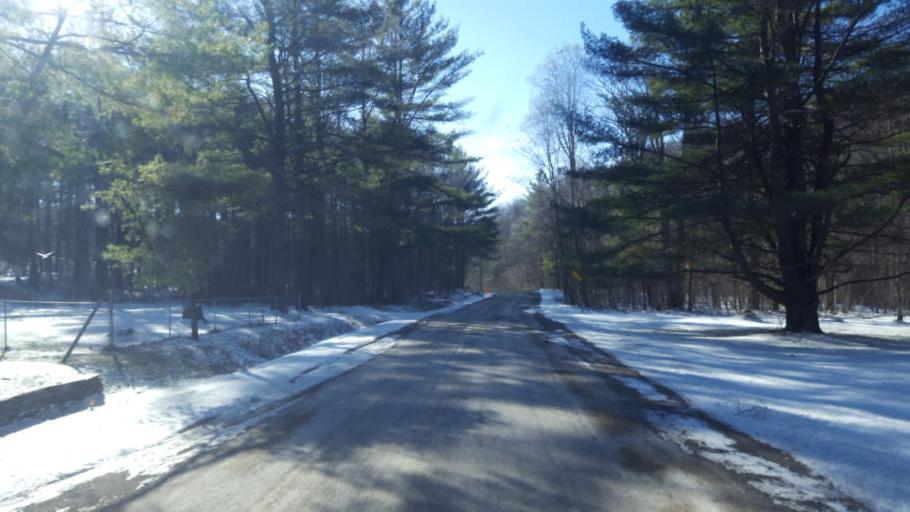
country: US
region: New York
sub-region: Allegany County
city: Wellsville
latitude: 42.1511
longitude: -77.9102
